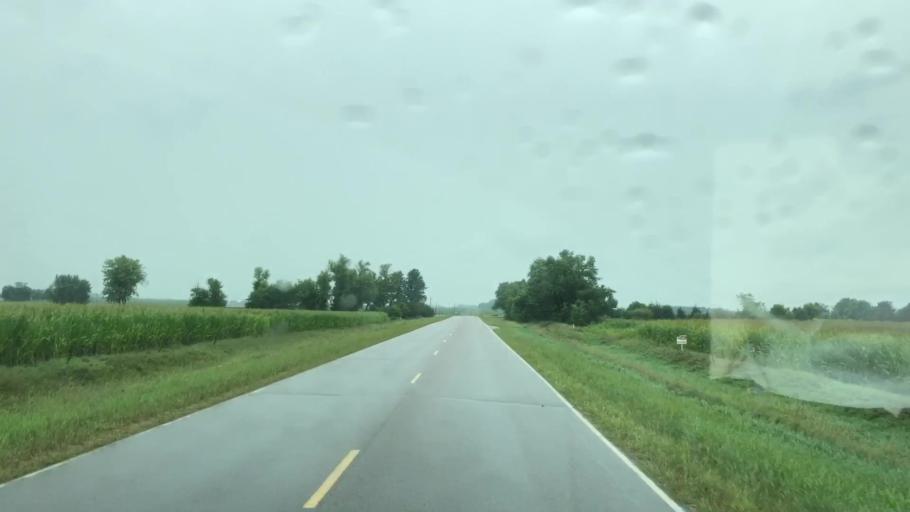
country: US
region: Iowa
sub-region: O'Brien County
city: Sanborn
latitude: 43.1921
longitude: -95.7230
